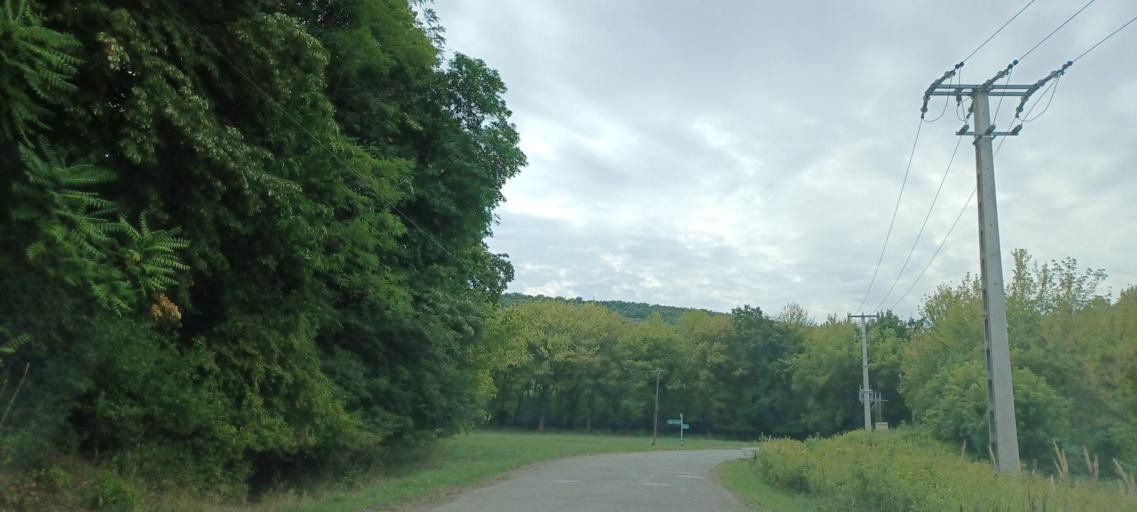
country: HU
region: Tolna
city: Szentgalpuszta
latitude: 46.3423
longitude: 18.6221
